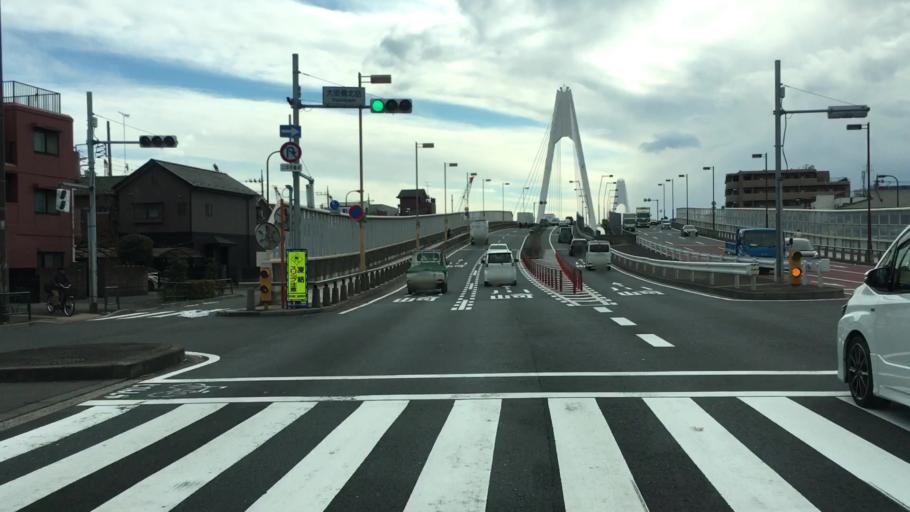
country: JP
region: Kanagawa
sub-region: Kawasaki-shi
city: Kawasaki
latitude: 35.5473
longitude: 139.7413
